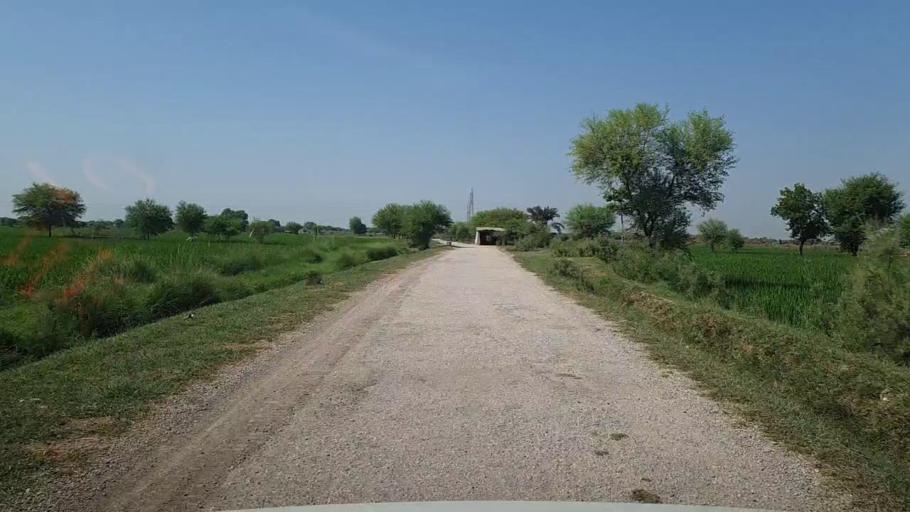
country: PK
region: Sindh
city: Kandhkot
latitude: 28.3322
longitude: 69.3672
